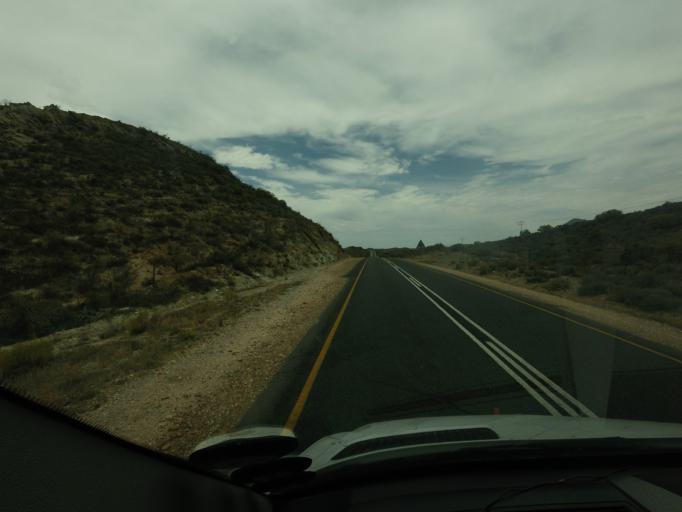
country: ZA
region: Western Cape
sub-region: Overberg District Municipality
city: Swellendam
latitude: -33.8523
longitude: 20.8159
